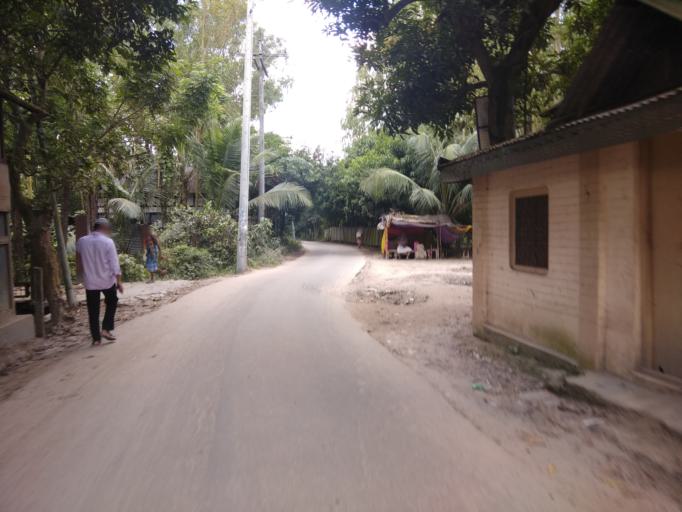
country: BD
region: Dhaka
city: Narayanganj
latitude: 23.4943
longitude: 90.4604
